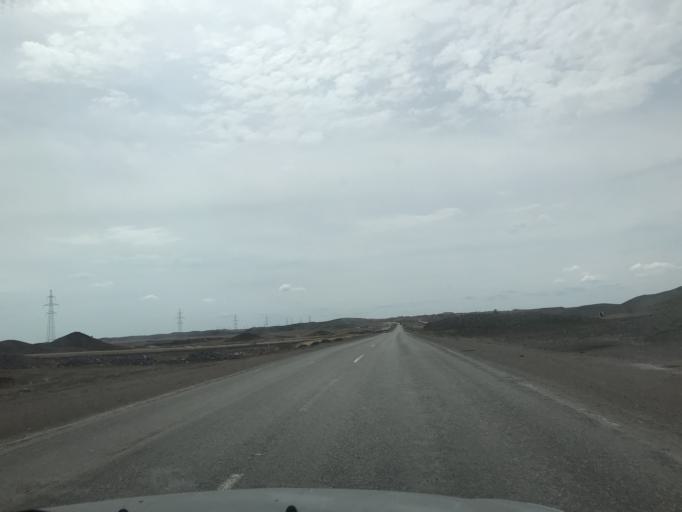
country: KZ
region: Zhambyl
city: Mynaral
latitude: 45.3852
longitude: 73.6499
